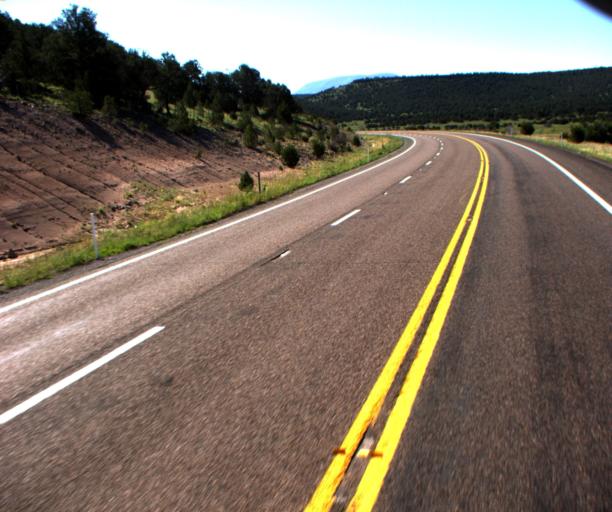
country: US
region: Arizona
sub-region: Apache County
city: Eagar
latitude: 34.0967
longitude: -109.2136
